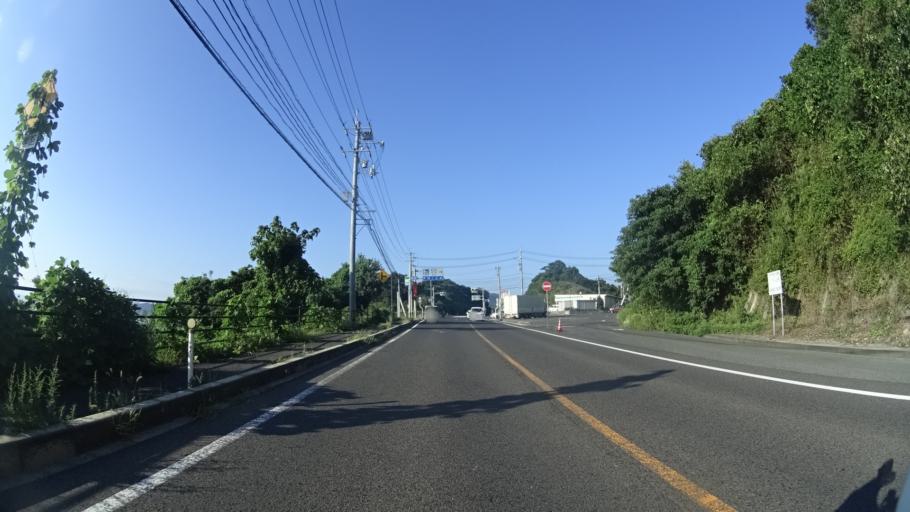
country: JP
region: Shimane
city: Matsue-shi
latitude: 35.5190
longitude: 133.1379
